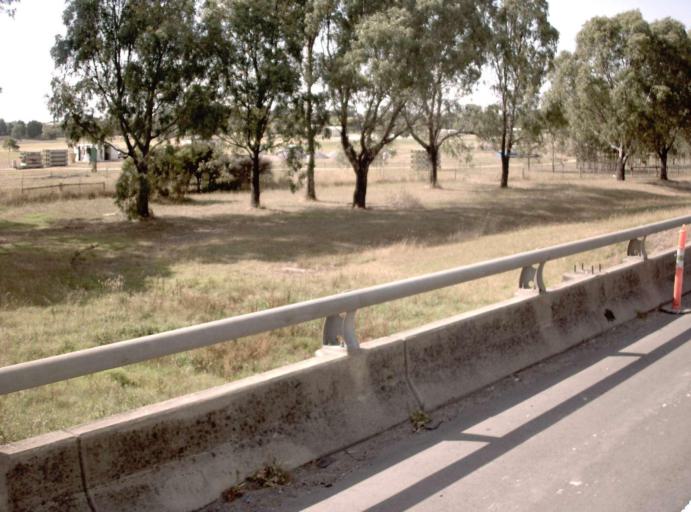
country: AU
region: Victoria
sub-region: Casey
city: Hampton Park
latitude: -38.0190
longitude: 145.2487
